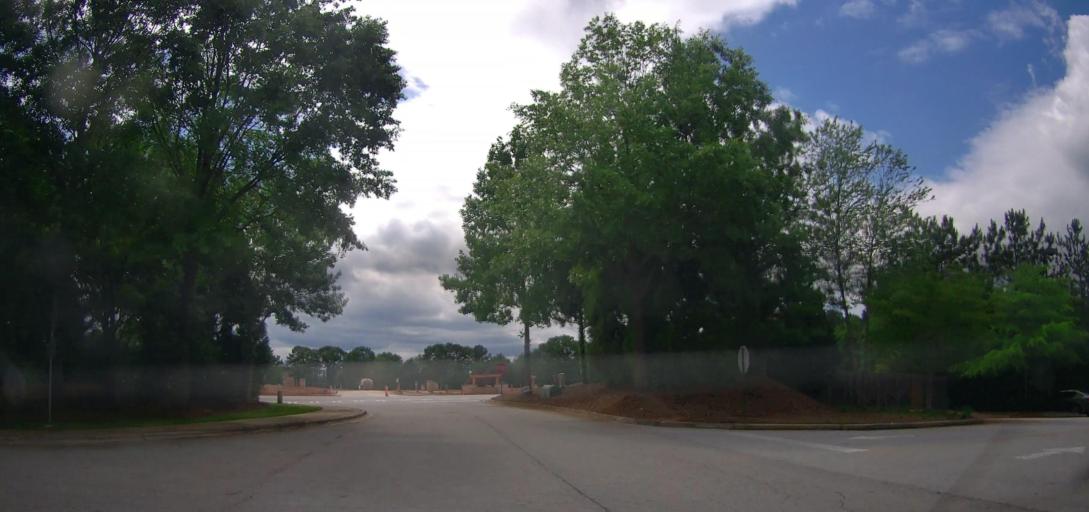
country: US
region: Georgia
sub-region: Rockdale County
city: Conyers
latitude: 33.6338
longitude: -84.0172
